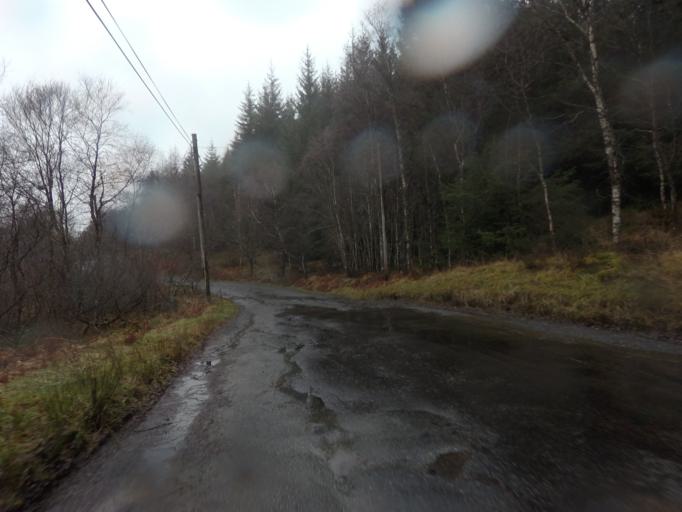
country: GB
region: Scotland
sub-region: West Dunbartonshire
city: Balloch
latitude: 56.1973
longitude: -4.5219
